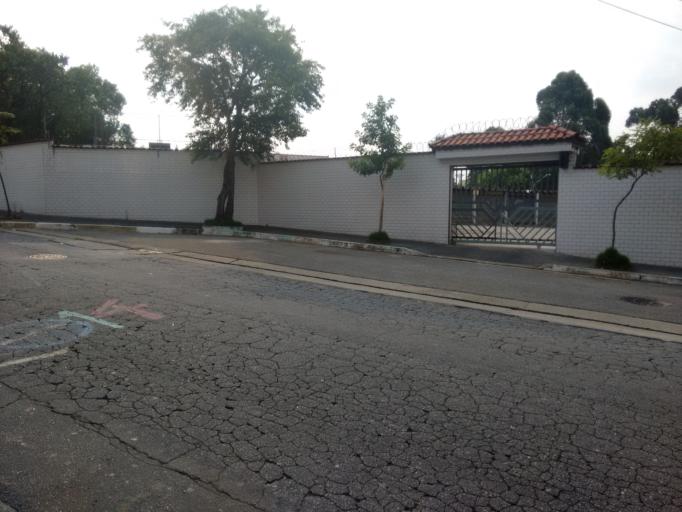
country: BR
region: Sao Paulo
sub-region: Guarulhos
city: Guarulhos
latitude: -23.5465
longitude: -46.4823
